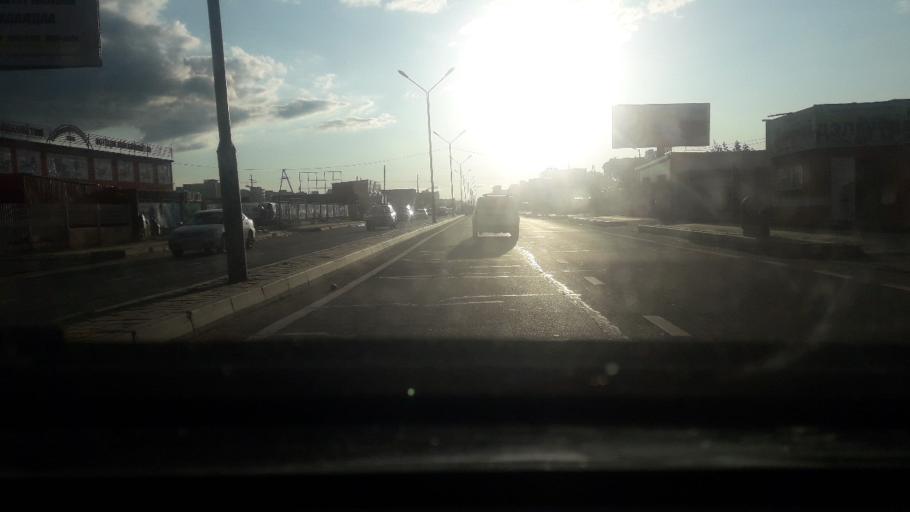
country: MN
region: Ulaanbaatar
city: Ulaanbaatar
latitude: 47.9079
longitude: 106.9637
